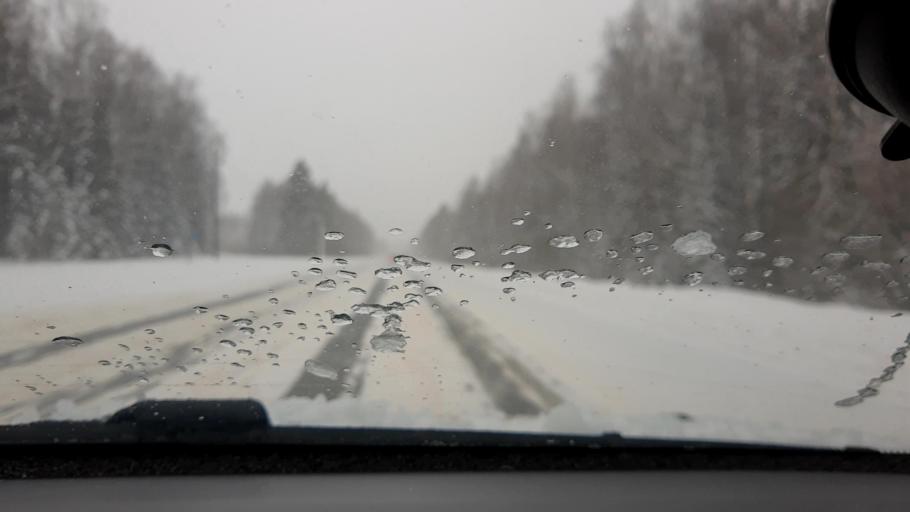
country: RU
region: Nizjnij Novgorod
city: Purekh
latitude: 56.6324
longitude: 43.1670
